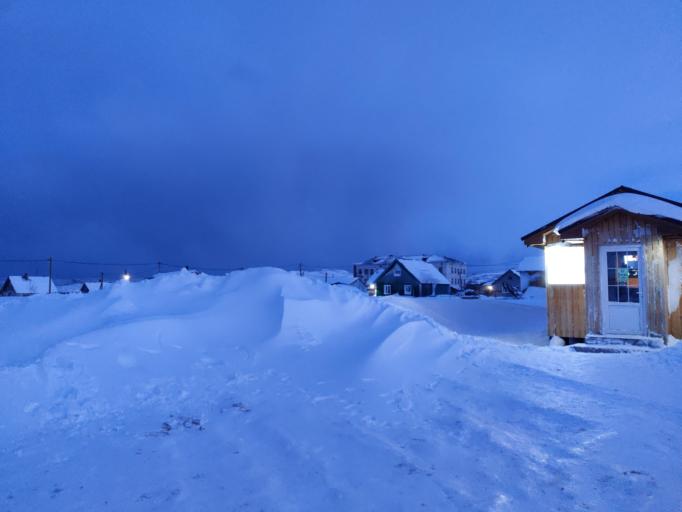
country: RU
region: Murmansk
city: Teriberka
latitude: 69.1639
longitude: 35.1465
